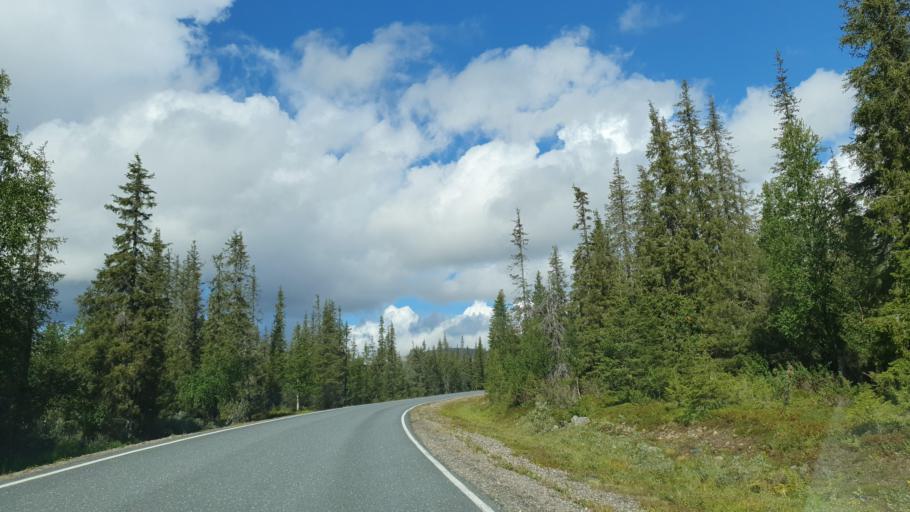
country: FI
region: Lapland
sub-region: Tunturi-Lappi
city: Muonio
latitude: 68.0360
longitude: 24.0662
